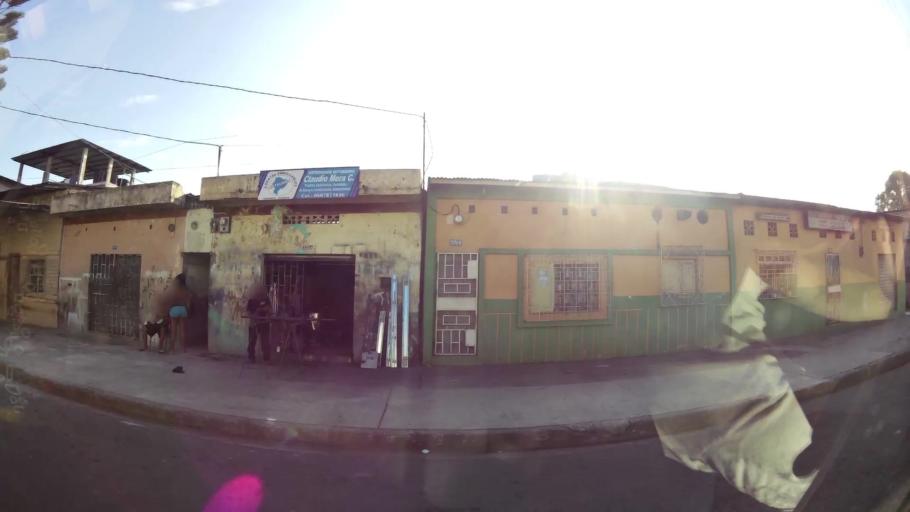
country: EC
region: Guayas
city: Guayaquil
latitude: -2.2157
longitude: -79.9085
